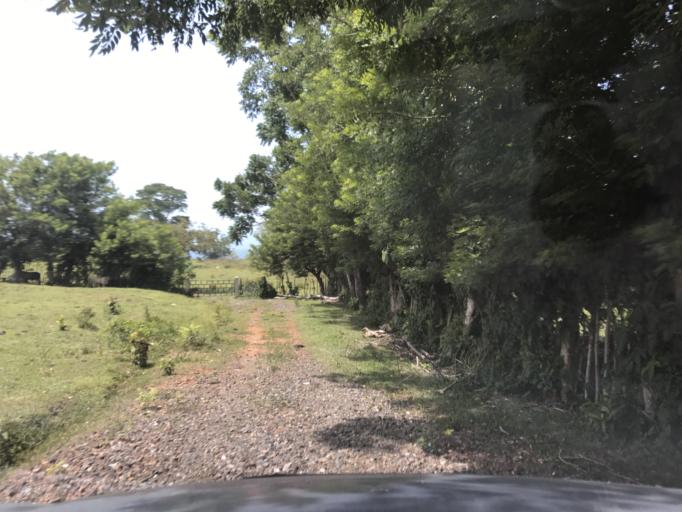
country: GT
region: Izabal
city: Morales
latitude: 15.6209
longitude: -89.0527
